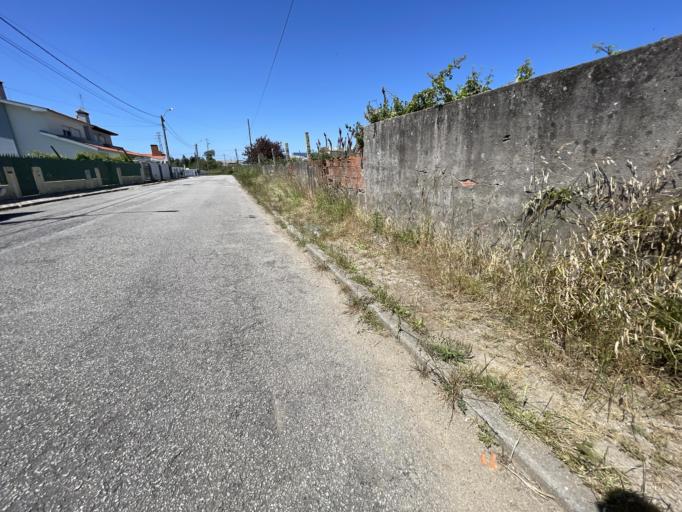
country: PT
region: Aveiro
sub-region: Ovar
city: Cortegaca
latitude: 40.9467
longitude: -8.6269
